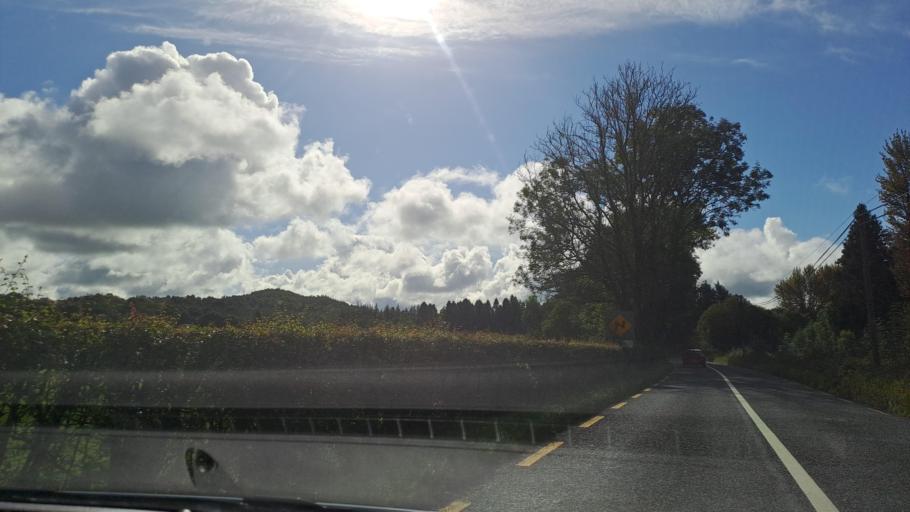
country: IE
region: Ulster
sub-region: An Cabhan
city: Kingscourt
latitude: 53.9160
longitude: -6.7855
